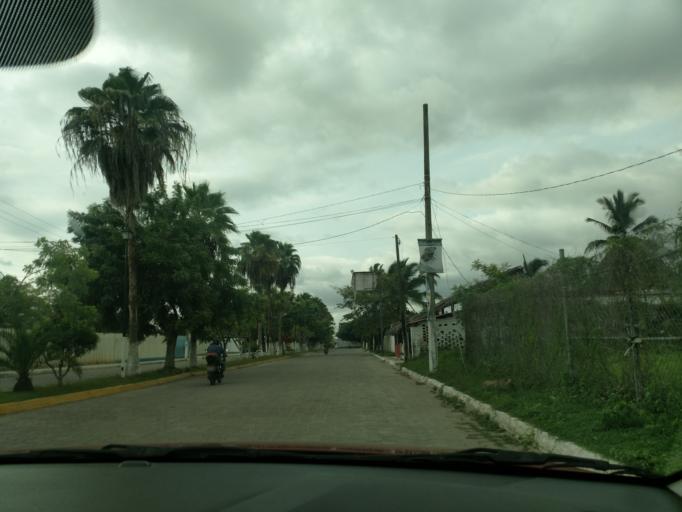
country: MX
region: Nayarit
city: San Blas
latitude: 21.5343
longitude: -105.2838
